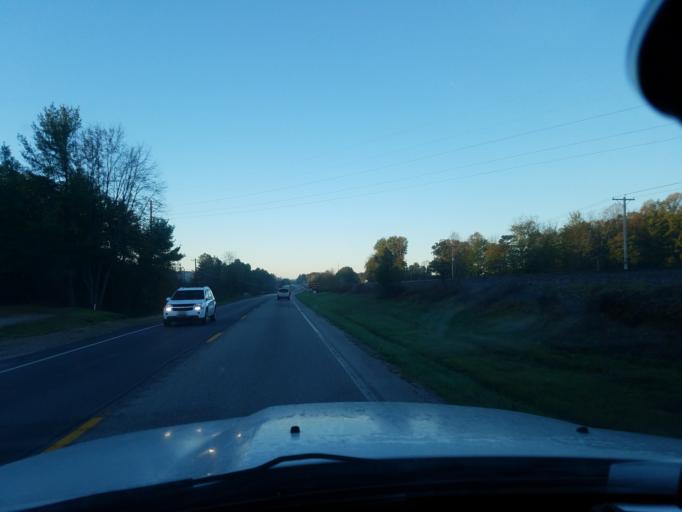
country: US
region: Kentucky
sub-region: Laurel County
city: North Corbin
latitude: 37.0385
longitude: -84.0577
